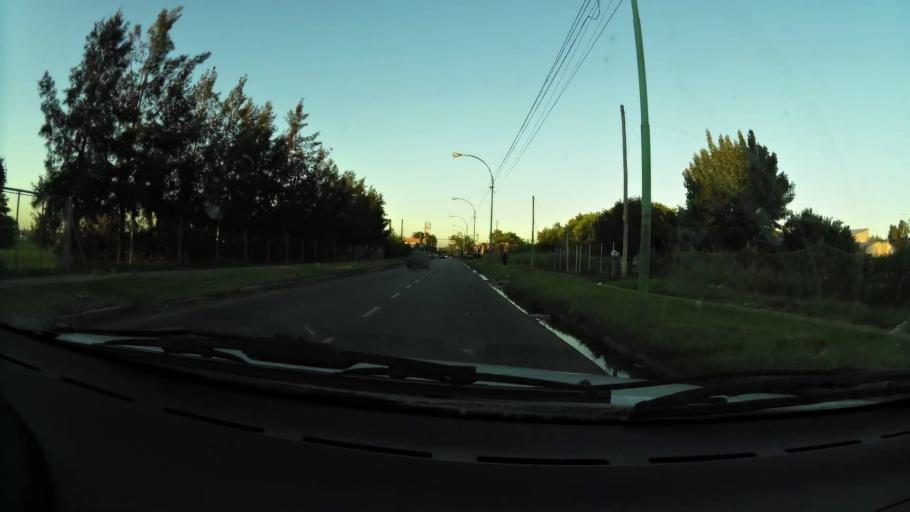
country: AR
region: Buenos Aires
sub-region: Partido de Quilmes
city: Quilmes
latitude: -34.8140
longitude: -58.1908
